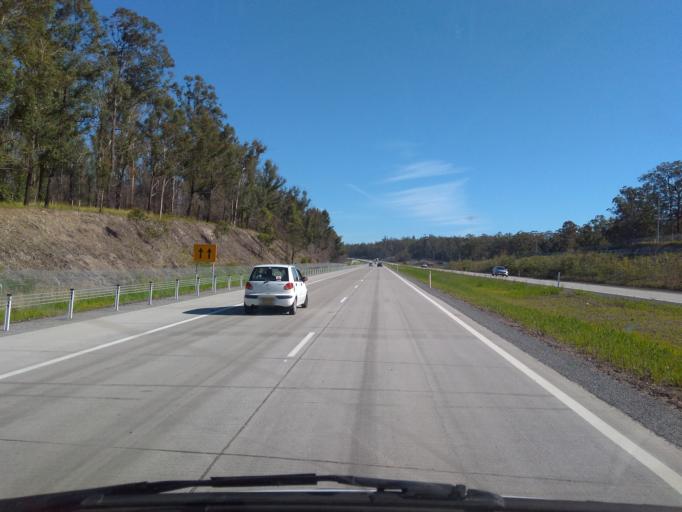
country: AU
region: New South Wales
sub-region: Kempsey
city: Kempsey
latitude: -31.1840
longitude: 152.8236
